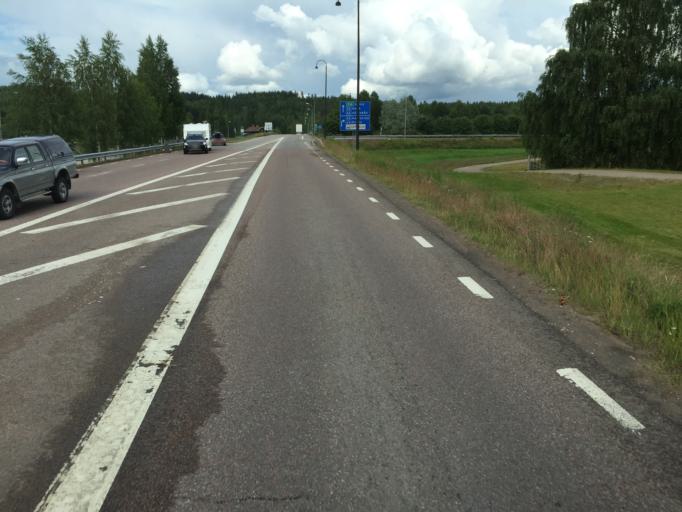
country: SE
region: Dalarna
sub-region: Vansbro Kommun
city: Vansbro
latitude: 60.5099
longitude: 14.2345
